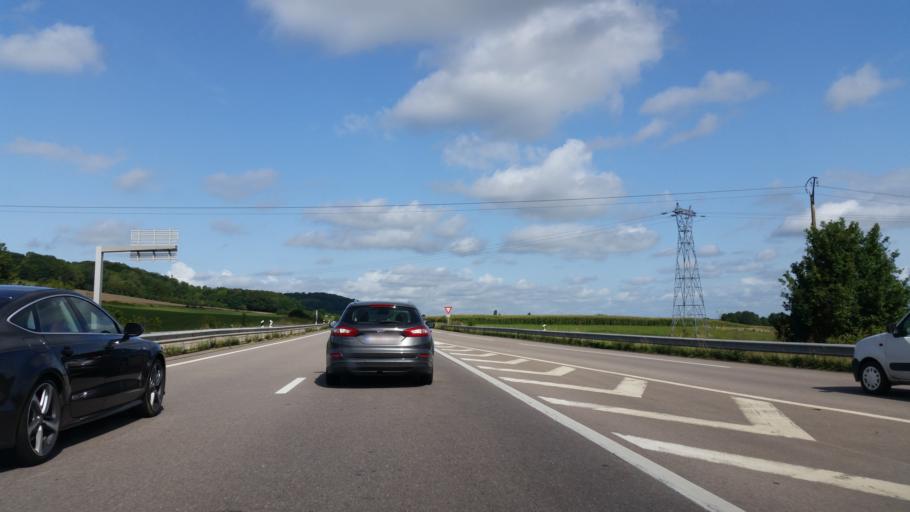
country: FR
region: Lorraine
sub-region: Departement des Vosges
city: Vincey
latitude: 48.3472
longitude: 6.3081
